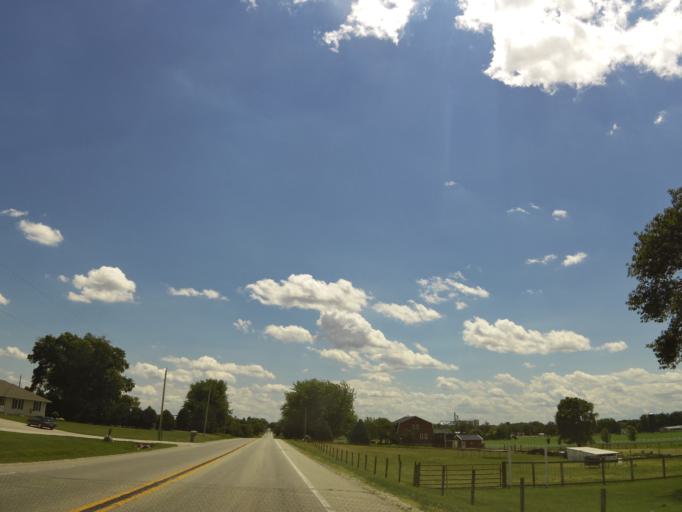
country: US
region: Iowa
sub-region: Buchanan County
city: Independence
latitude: 42.4885
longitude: -91.8895
